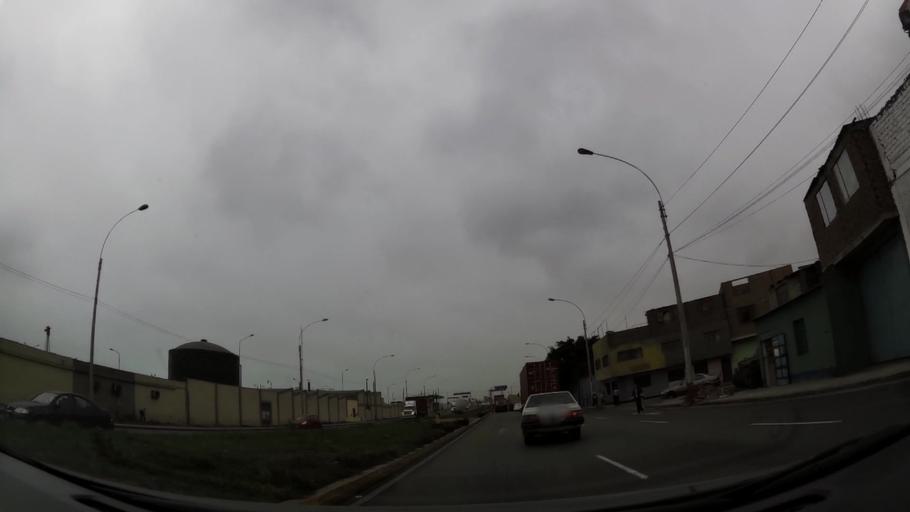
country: PE
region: Callao
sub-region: Callao
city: Callao
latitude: -12.0402
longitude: -77.1269
